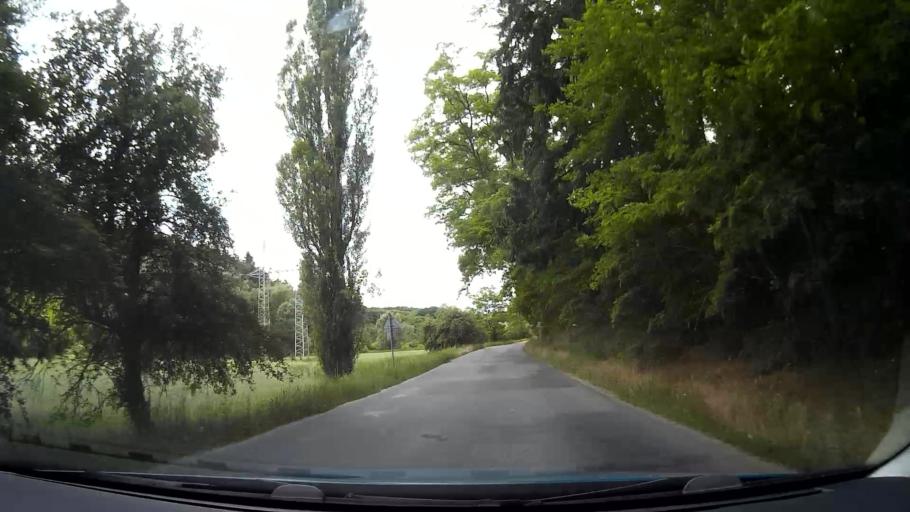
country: CZ
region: South Moravian
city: Ostopovice
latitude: 49.1461
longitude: 16.5296
